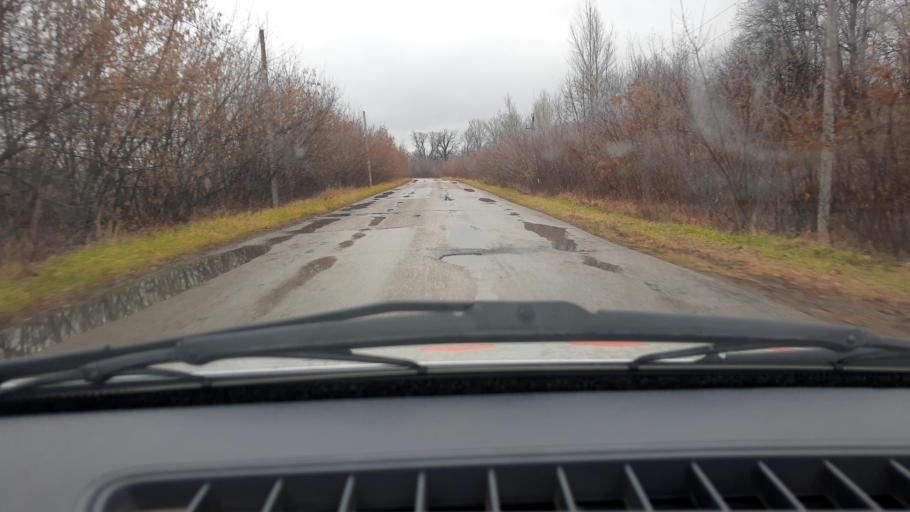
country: RU
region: Bashkortostan
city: Iglino
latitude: 54.8055
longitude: 56.1930
